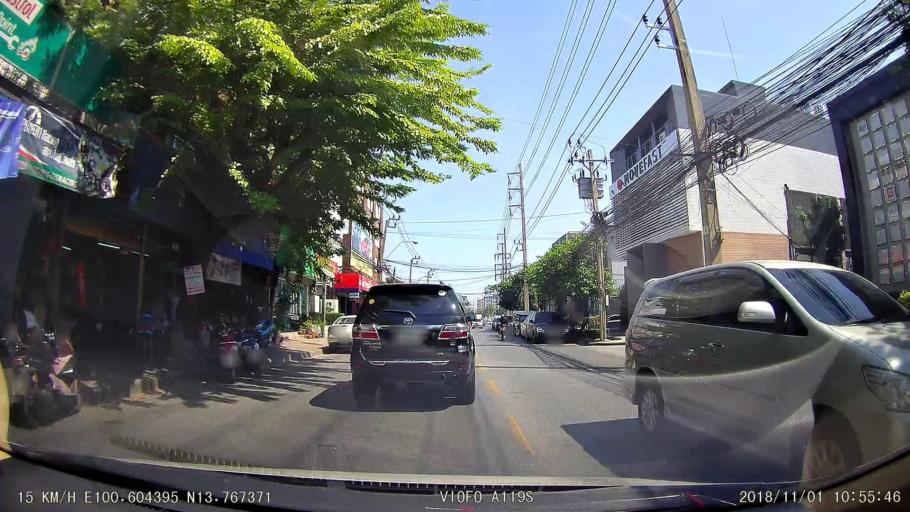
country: TH
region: Bangkok
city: Wang Thonglang
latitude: 13.7676
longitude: 100.6045
